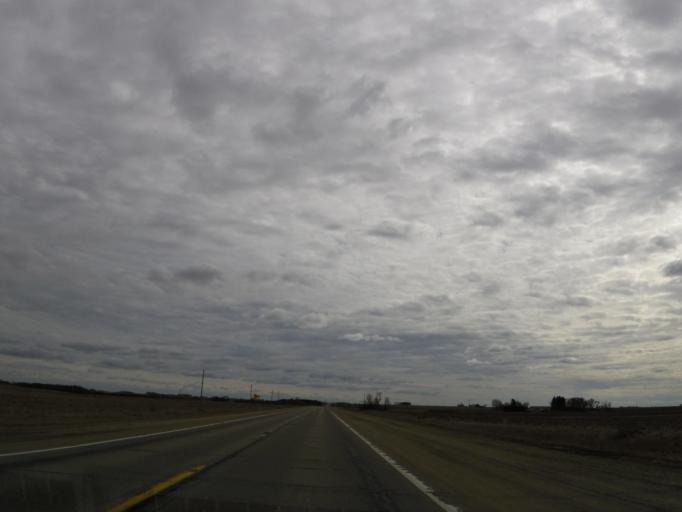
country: US
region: Iowa
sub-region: Howard County
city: Cresco
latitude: 43.4031
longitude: -92.2985
